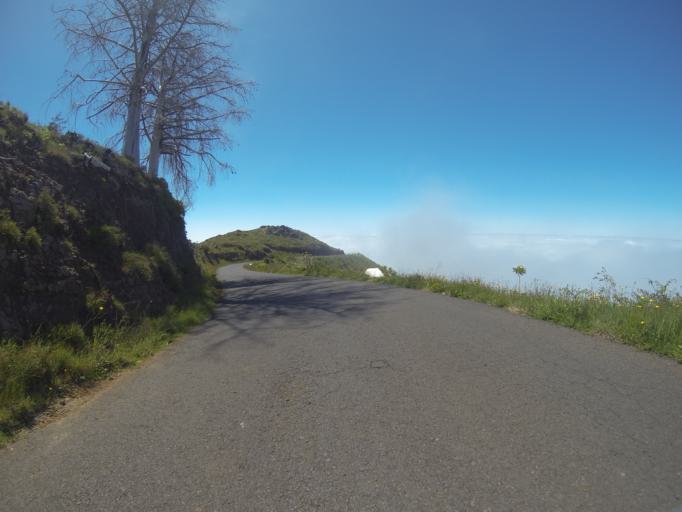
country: PT
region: Madeira
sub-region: Funchal
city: Nossa Senhora do Monte
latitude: 32.7017
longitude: -16.9152
